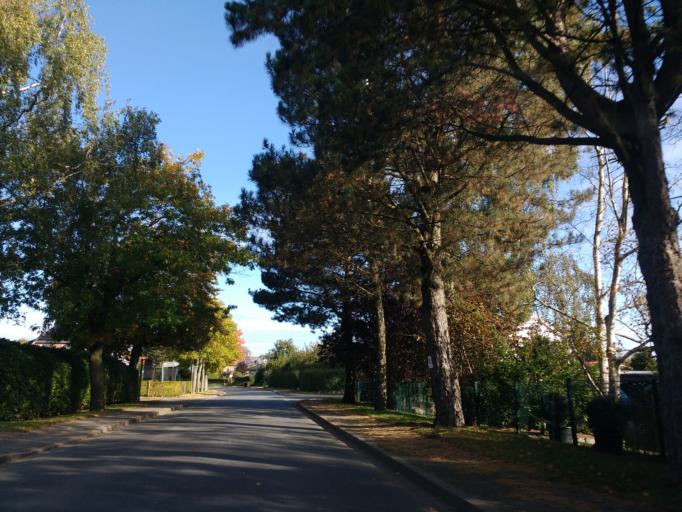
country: DE
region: Schleswig-Holstein
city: Wangels
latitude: 54.2535
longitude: 10.7510
